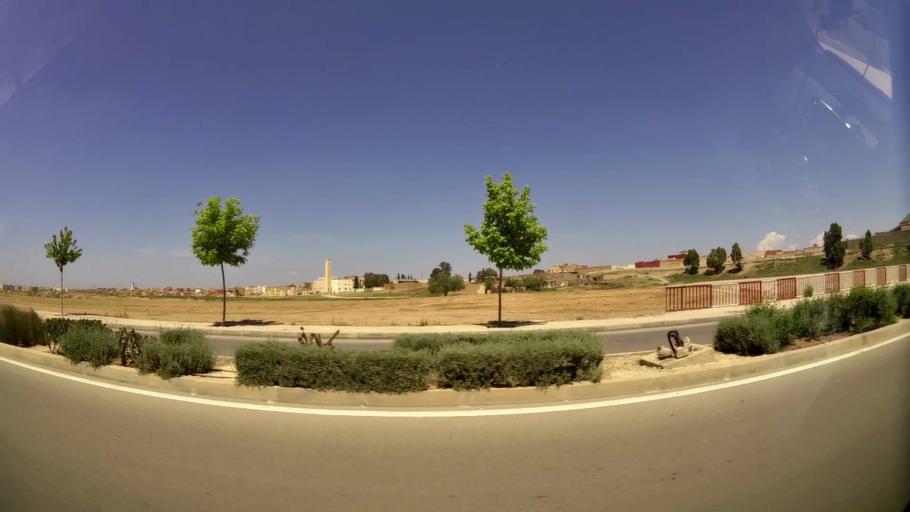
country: MA
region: Oriental
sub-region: Oujda-Angad
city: Oujda
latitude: 34.6936
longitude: -1.9251
